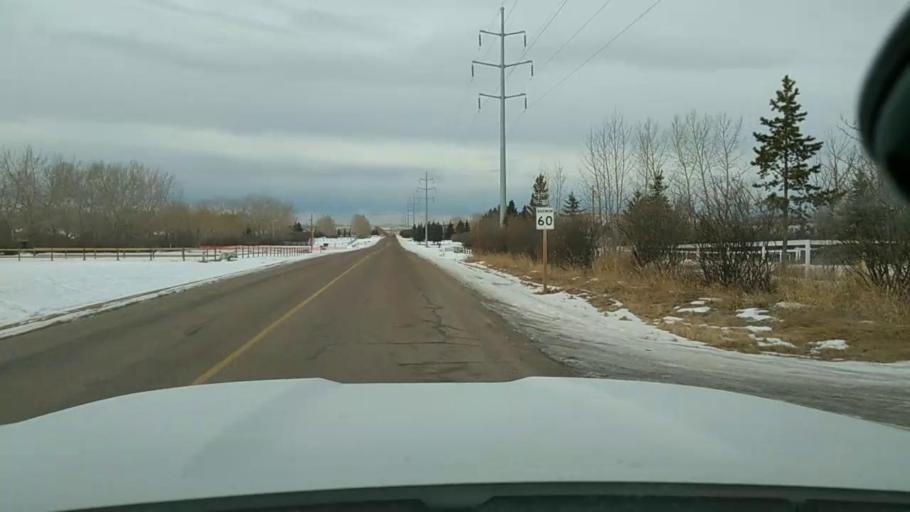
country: CA
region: Alberta
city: Airdrie
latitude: 51.2417
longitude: -113.9731
